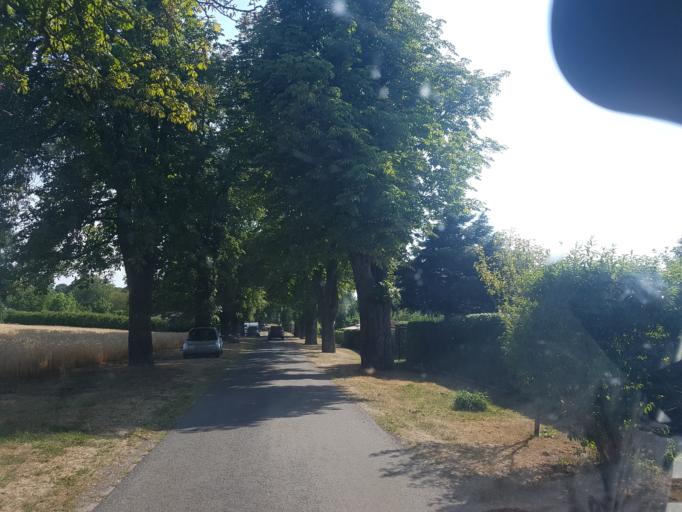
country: DE
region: Brandenburg
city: Ludwigsfelde
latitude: 52.2737
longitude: 13.2854
